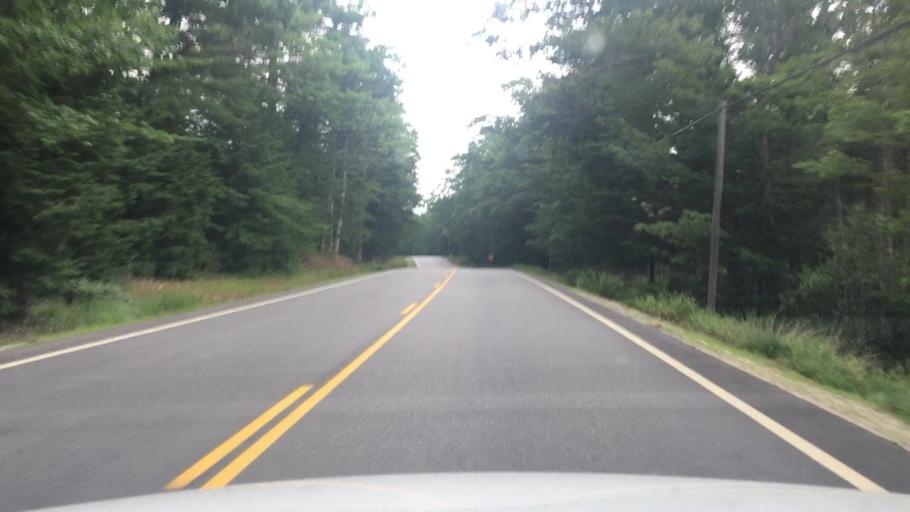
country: US
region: Maine
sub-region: Oxford County
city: Hartford
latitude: 44.3746
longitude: -70.4052
